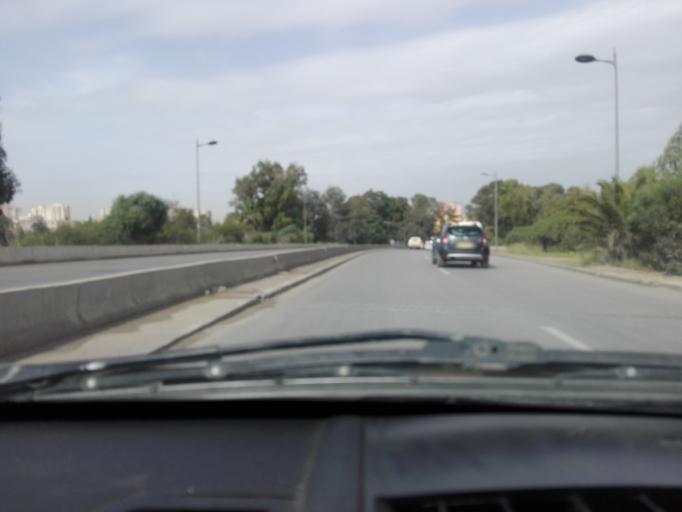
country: DZ
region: Alger
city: Bab Ezzouar
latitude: 36.7253
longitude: 3.1966
